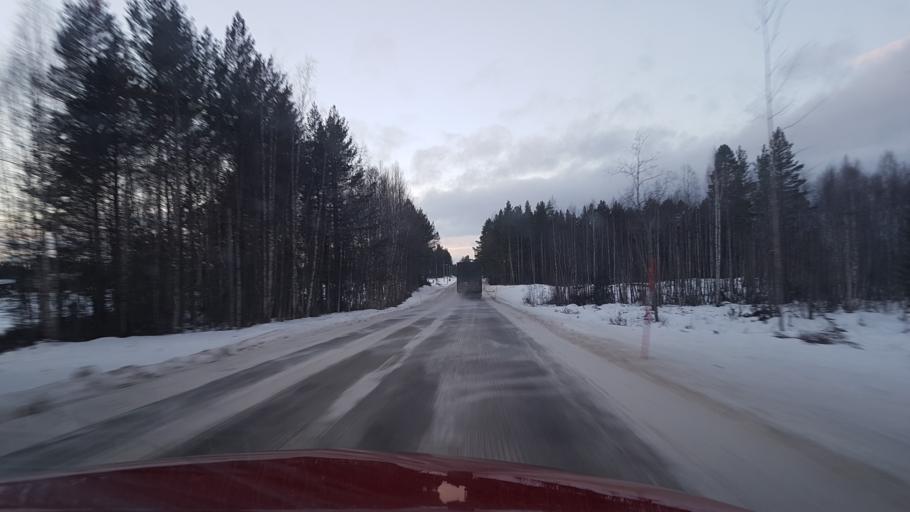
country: SE
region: Jaemtland
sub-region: Harjedalens Kommun
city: Sveg
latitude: 62.0263
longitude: 14.4369
